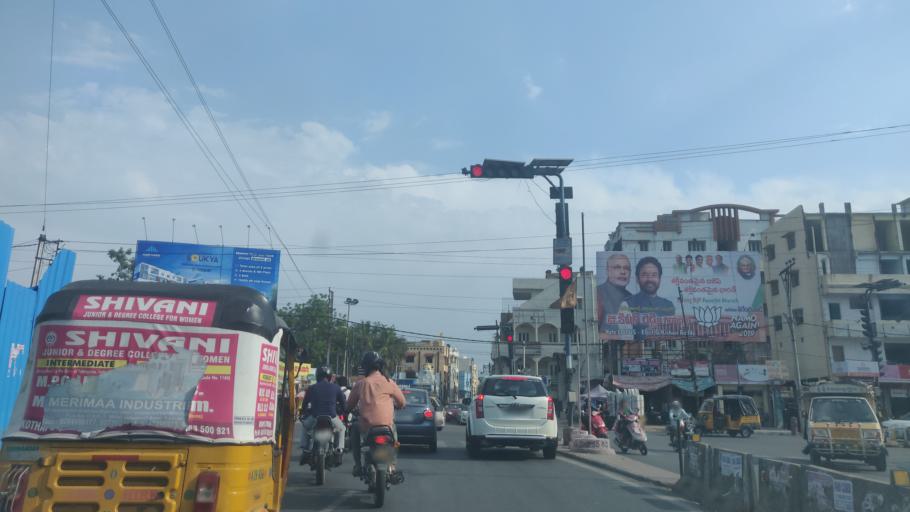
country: IN
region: Telangana
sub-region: Rangareddi
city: Gaddi Annaram
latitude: 17.3916
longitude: 78.5109
